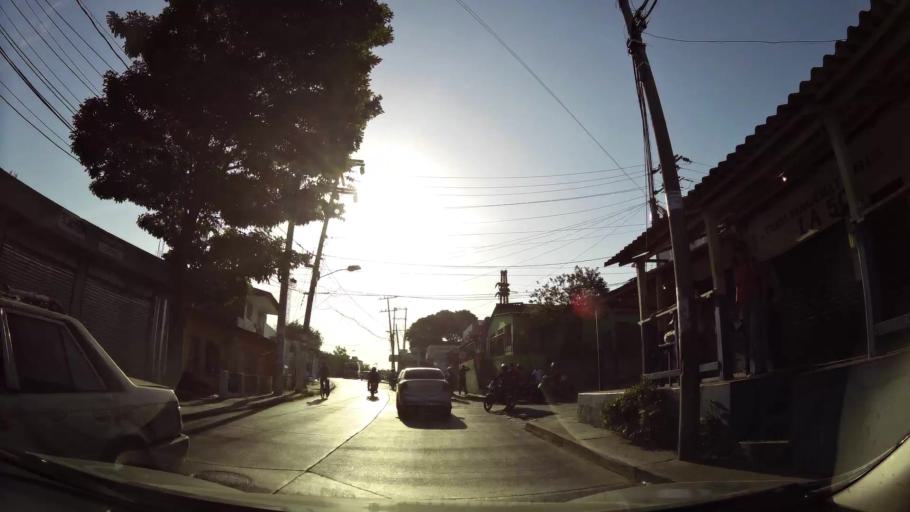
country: CO
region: Bolivar
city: Cartagena
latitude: 10.4040
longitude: -75.5067
